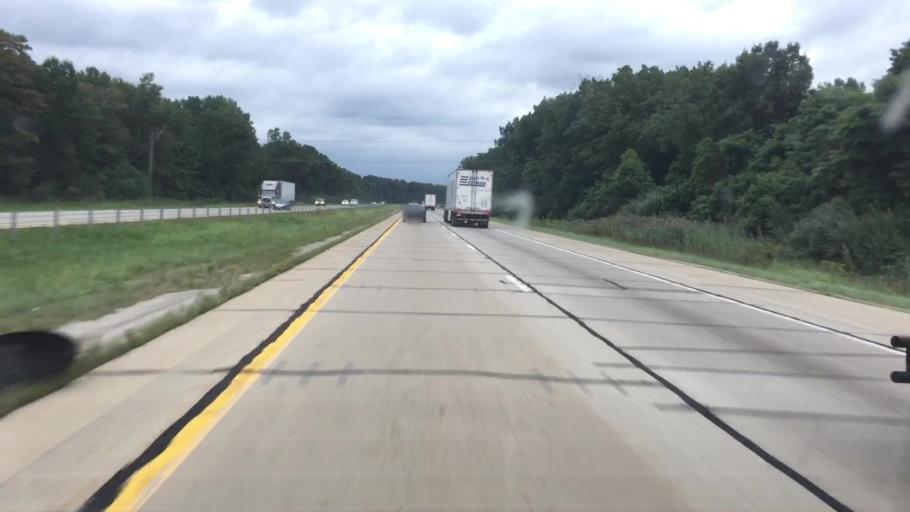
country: US
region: Michigan
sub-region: Monroe County
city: Petersburg
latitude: 41.8635
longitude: -83.6612
